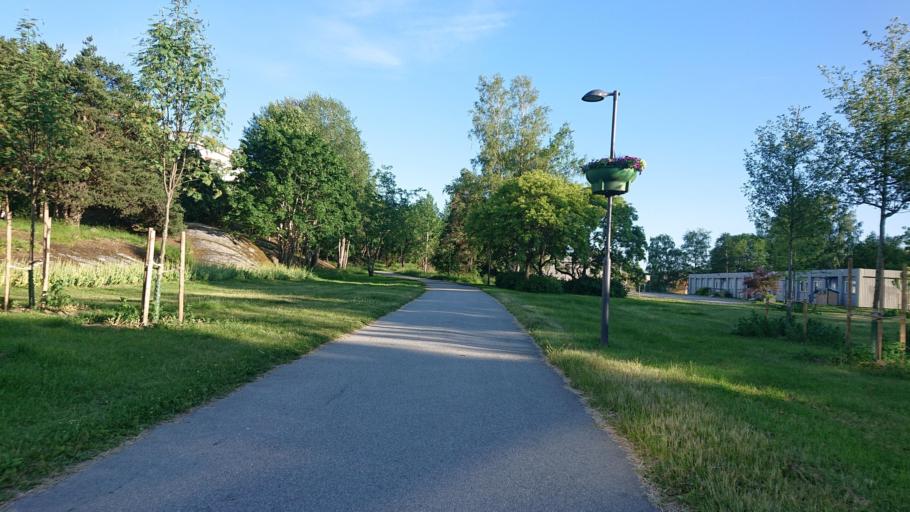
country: SE
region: Stockholm
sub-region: Osterakers Kommun
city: Akersberga
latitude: 59.4835
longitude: 18.3054
